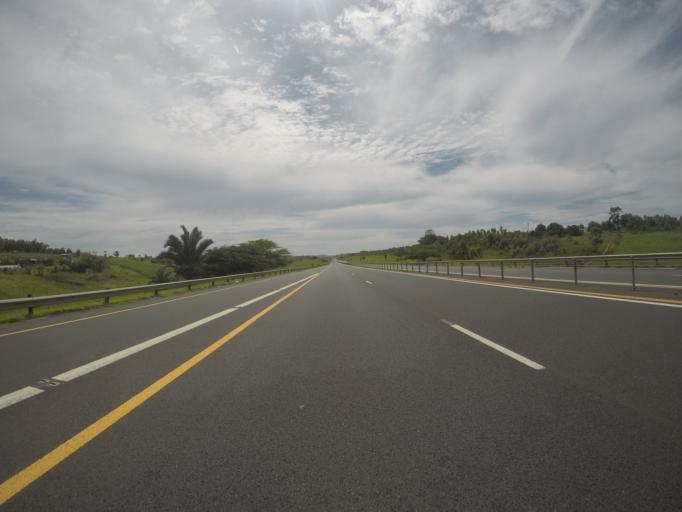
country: ZA
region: KwaZulu-Natal
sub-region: iLembe District Municipality
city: Mandeni
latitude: -29.1826
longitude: 31.4881
